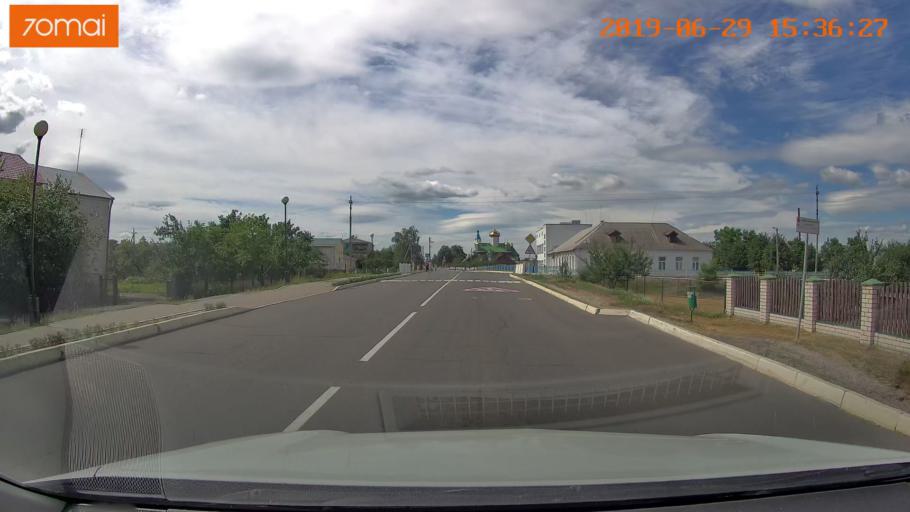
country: BY
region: Brest
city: Mikashevichy
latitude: 52.2206
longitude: 27.4681
